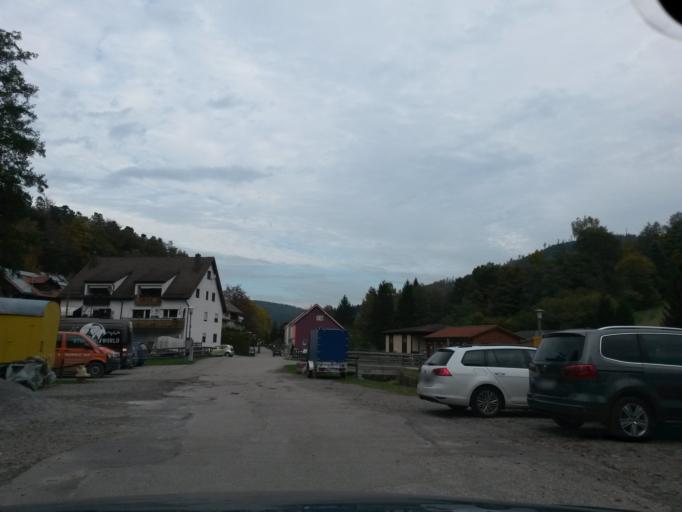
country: DE
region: Baden-Wuerttemberg
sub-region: Karlsruhe Region
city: Bad Herrenalb
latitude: 48.7924
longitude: 8.4284
